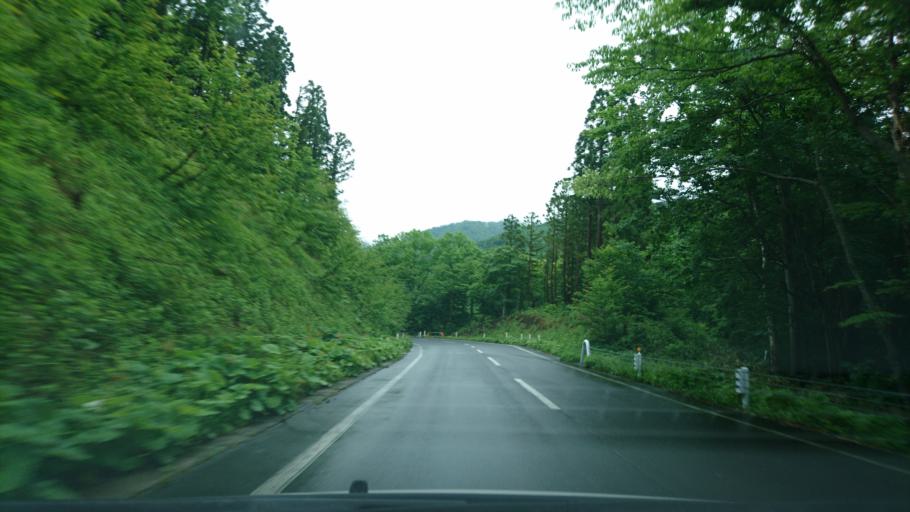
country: JP
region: Iwate
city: Ichinoseki
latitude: 39.0027
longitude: 140.8360
